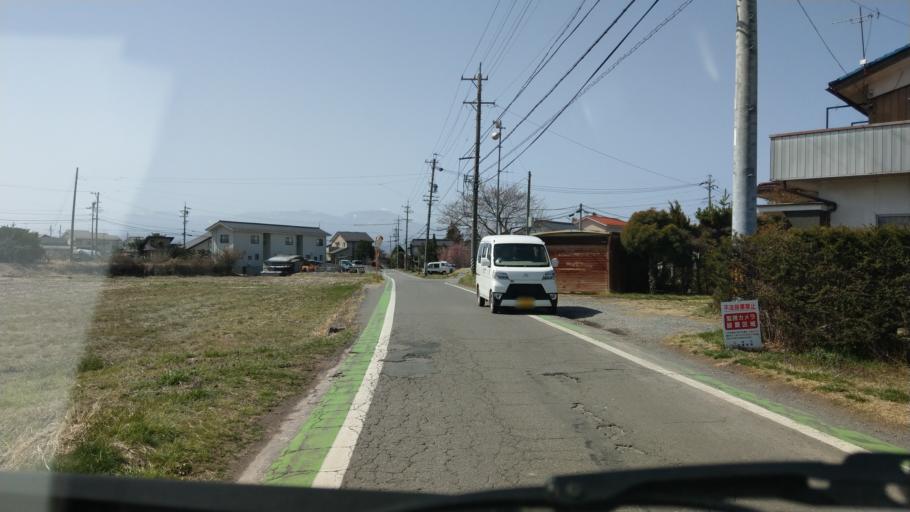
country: JP
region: Nagano
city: Komoro
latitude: 36.3002
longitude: 138.4445
